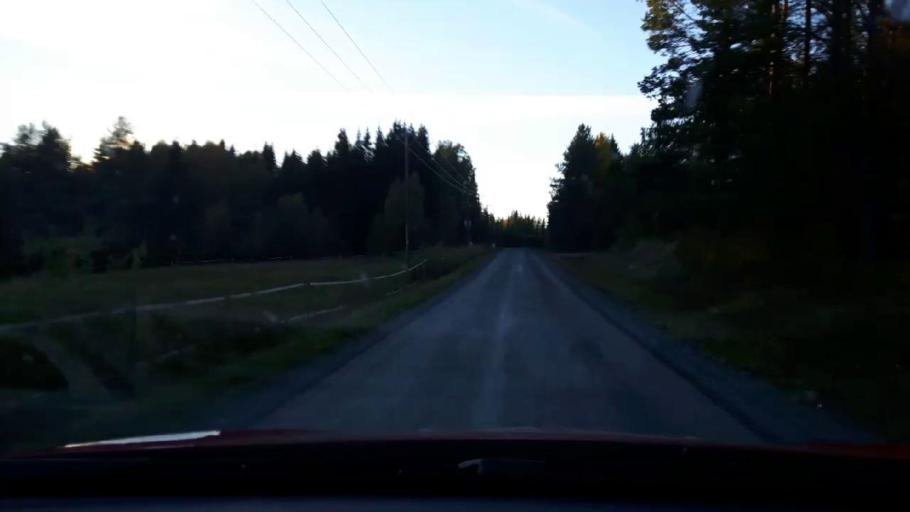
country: SE
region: Jaemtland
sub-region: Krokoms Kommun
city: Krokom
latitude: 63.4323
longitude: 14.4322
